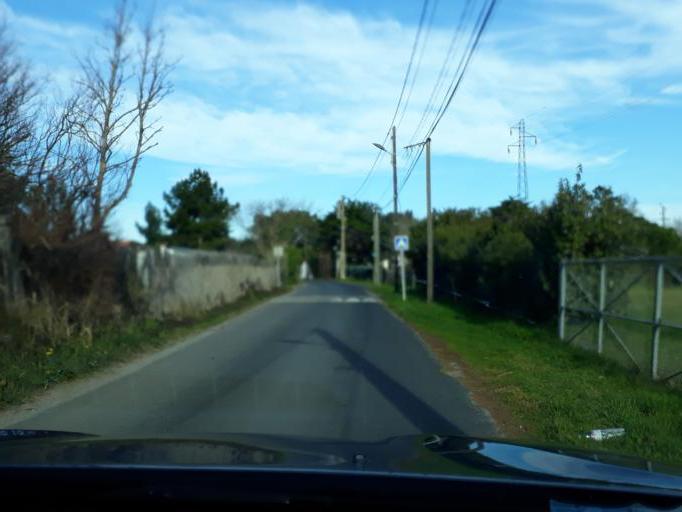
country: FR
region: Languedoc-Roussillon
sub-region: Departement de l'Herault
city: Marseillan
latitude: 43.3223
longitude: 3.5423
